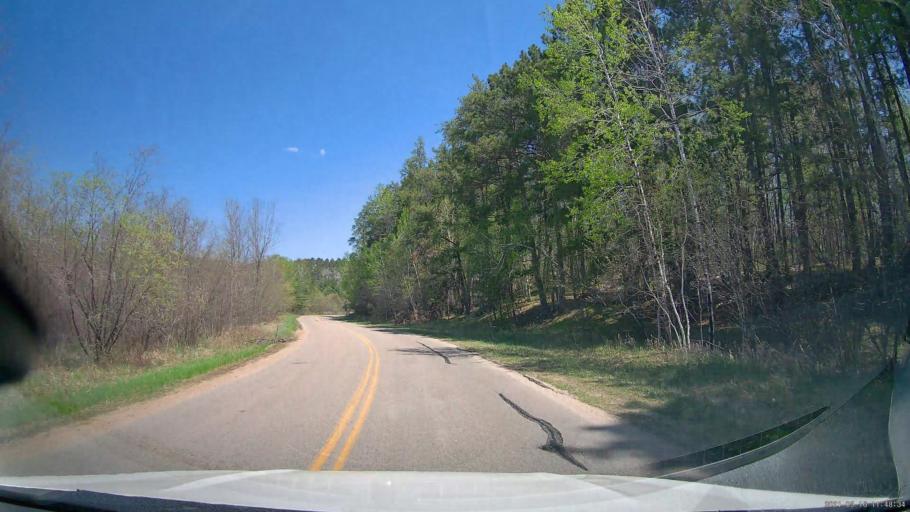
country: US
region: Minnesota
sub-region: Hubbard County
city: Park Rapids
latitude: 46.9830
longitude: -94.9503
